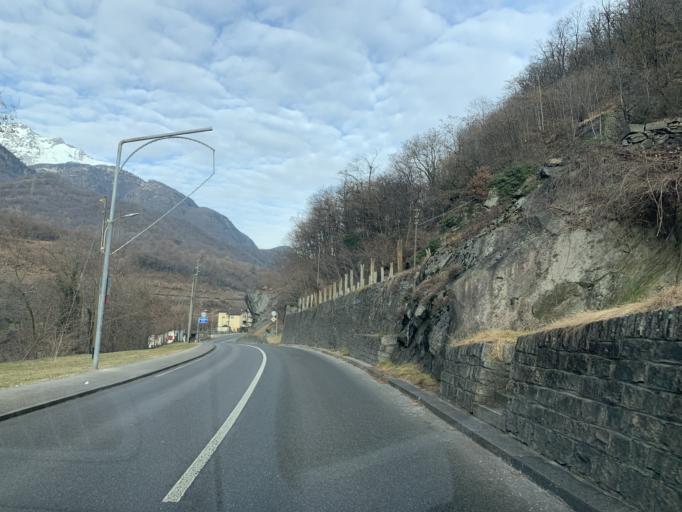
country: CH
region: Ticino
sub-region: Leventina District
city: Bodio
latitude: 46.4043
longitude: 8.8735
